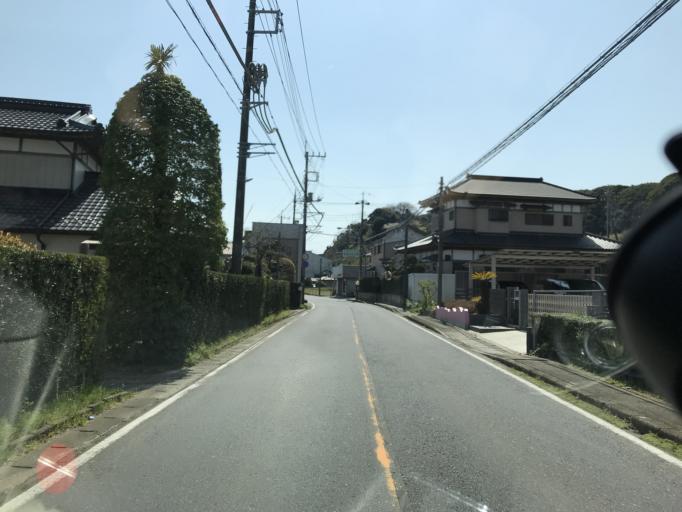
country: JP
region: Chiba
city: Asahi
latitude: 35.7815
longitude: 140.6504
